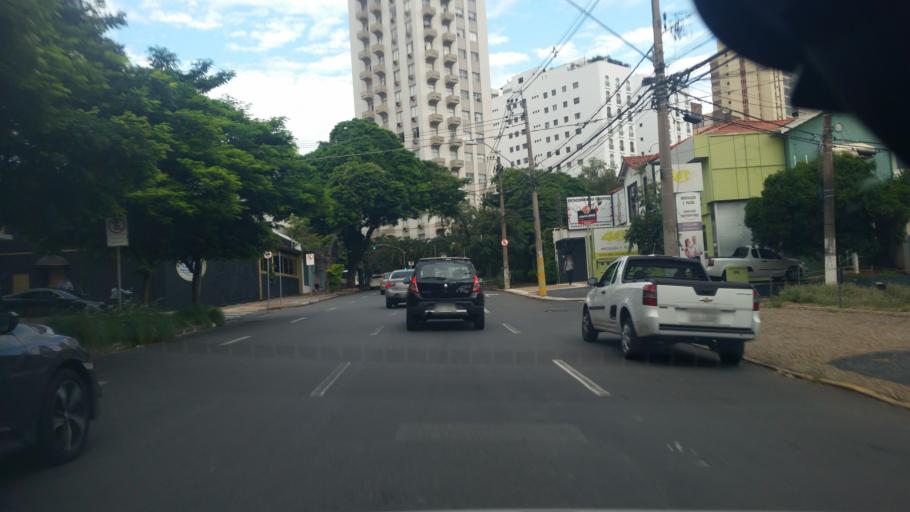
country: BR
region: Sao Paulo
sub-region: Campinas
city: Campinas
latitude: -22.8958
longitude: -47.0580
